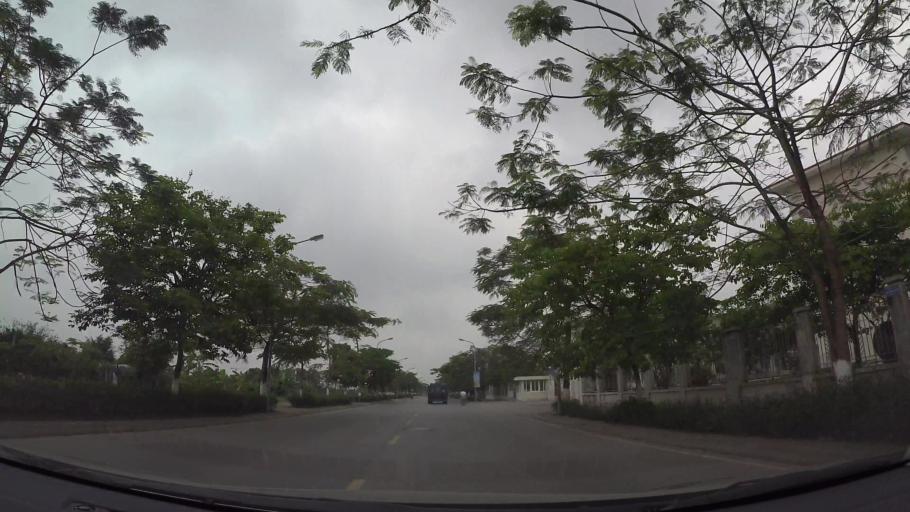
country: VN
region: Ha Noi
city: Trau Quy
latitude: 21.0444
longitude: 105.9248
